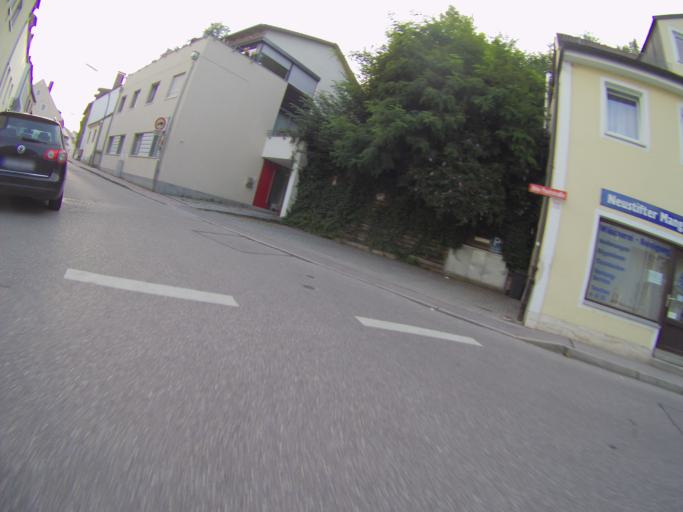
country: DE
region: Bavaria
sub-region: Upper Bavaria
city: Freising
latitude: 48.4060
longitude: 11.7558
